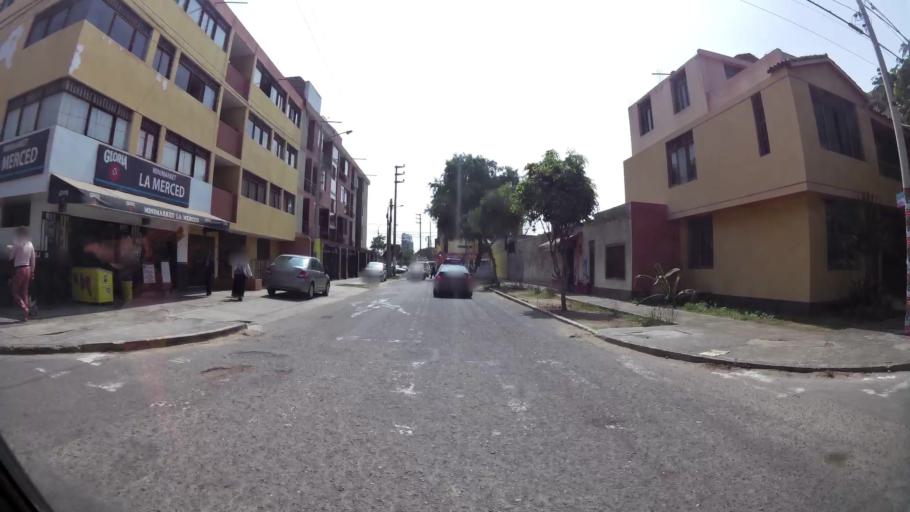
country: PE
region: La Libertad
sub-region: Provincia de Trujillo
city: Buenos Aires
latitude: -8.1260
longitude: -79.0392
